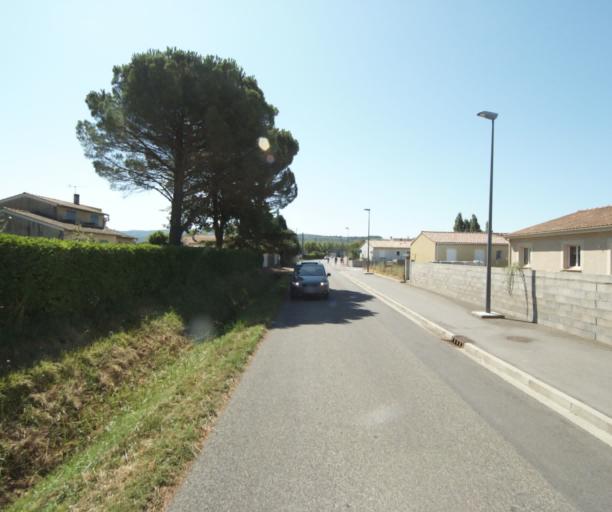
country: FR
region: Midi-Pyrenees
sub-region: Departement de la Haute-Garonne
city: Revel
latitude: 43.4659
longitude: 1.9953
